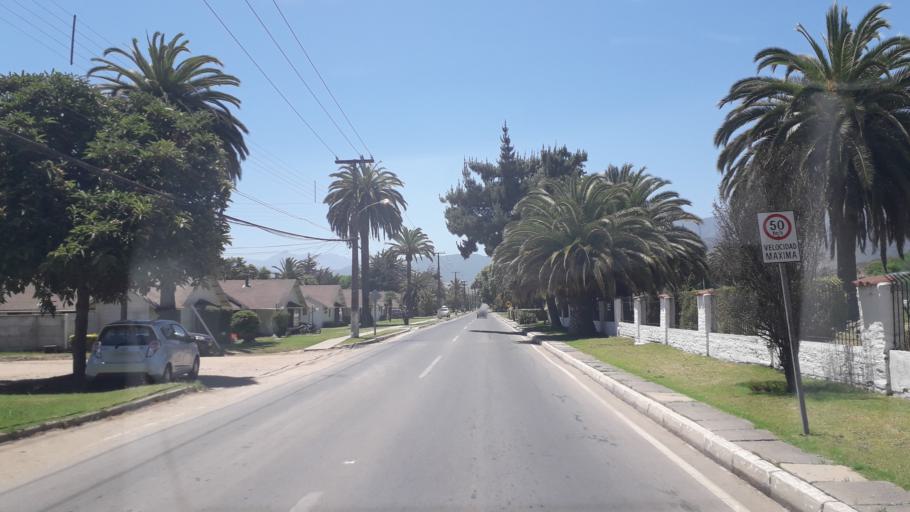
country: CL
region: Valparaiso
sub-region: Provincia de Quillota
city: Quillota
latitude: -32.9144
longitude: -71.2321
